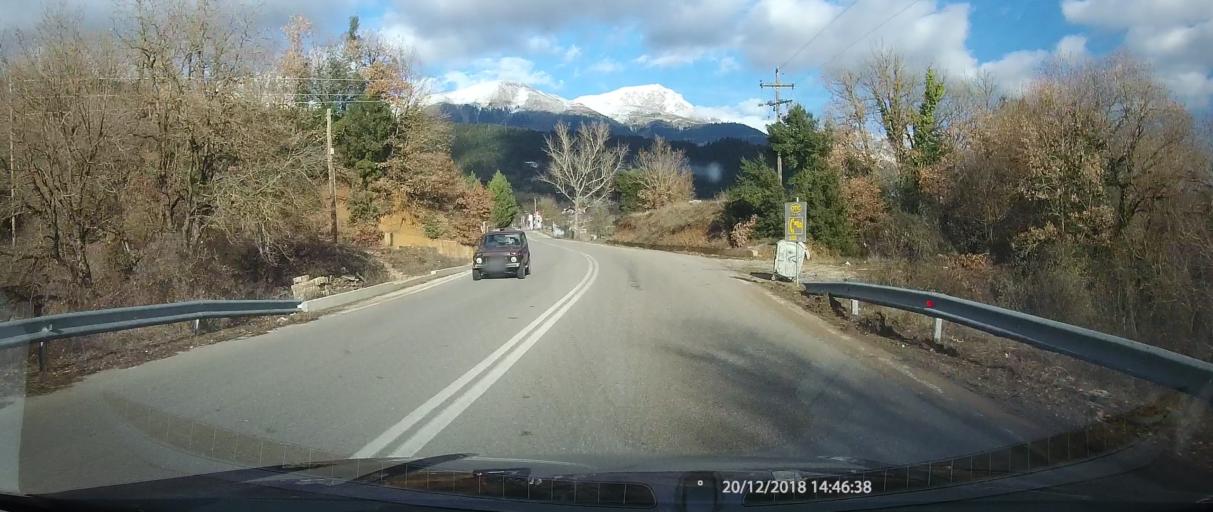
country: GR
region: Central Greece
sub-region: Nomos Evrytanias
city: Karpenisi
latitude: 38.8977
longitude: 21.7695
